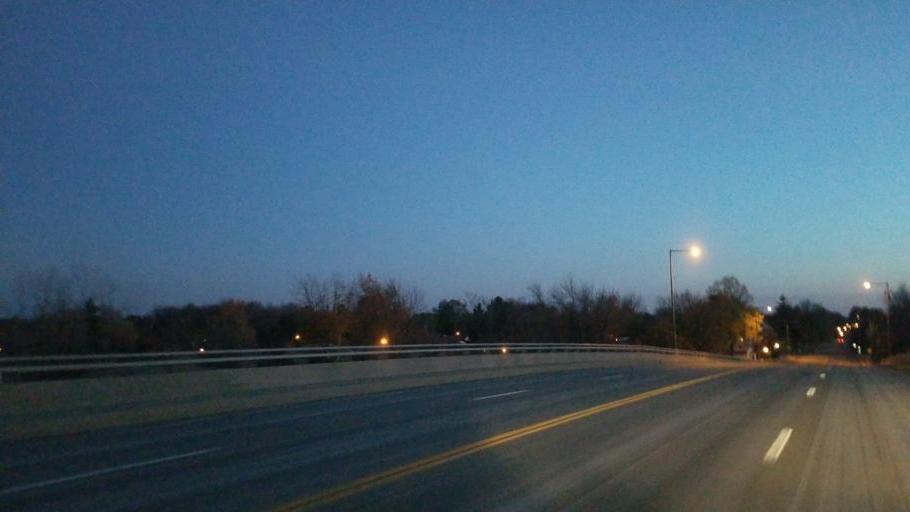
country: US
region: Ohio
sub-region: Crawford County
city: Crestline
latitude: 40.7820
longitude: -82.7383
